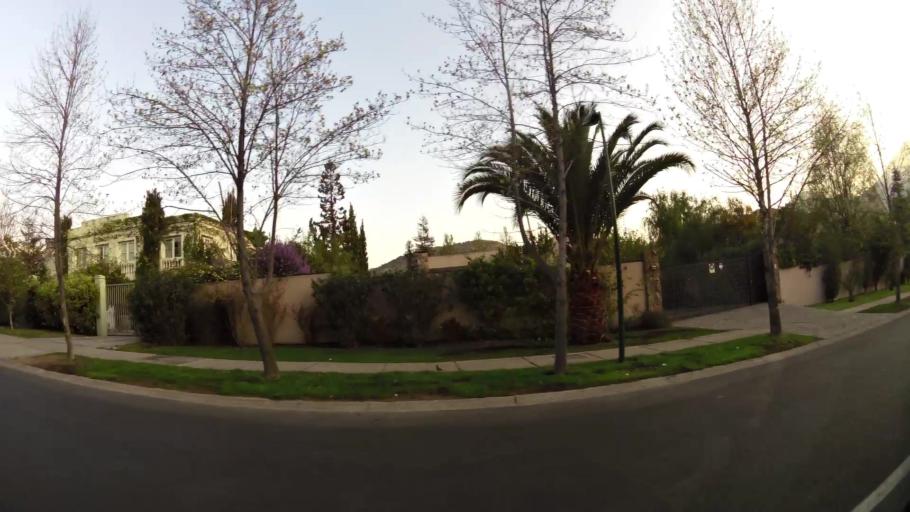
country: CL
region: Santiago Metropolitan
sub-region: Provincia de Chacabuco
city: Chicureo Abajo
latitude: -33.3321
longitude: -70.5403
